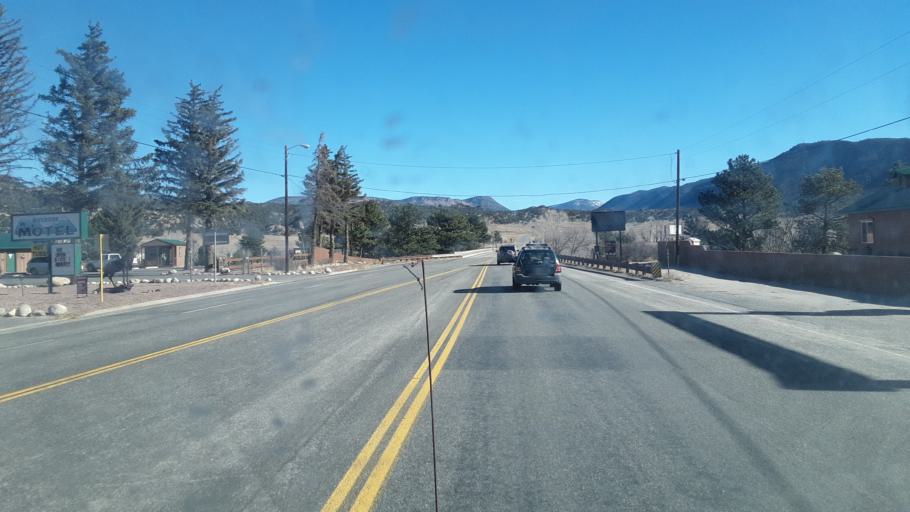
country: US
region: Colorado
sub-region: Chaffee County
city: Buena Vista
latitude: 38.8127
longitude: -106.1056
